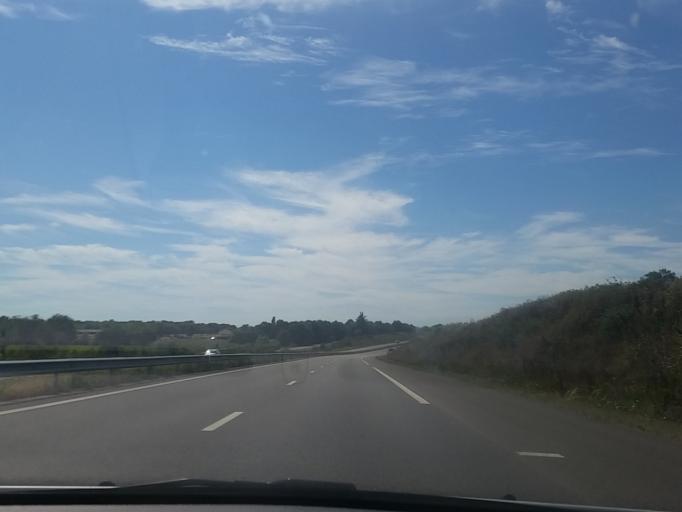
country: FR
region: Pays de la Loire
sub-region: Departement de la Loire-Atlantique
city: Le Pellerin
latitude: 47.1841
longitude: -1.7597
